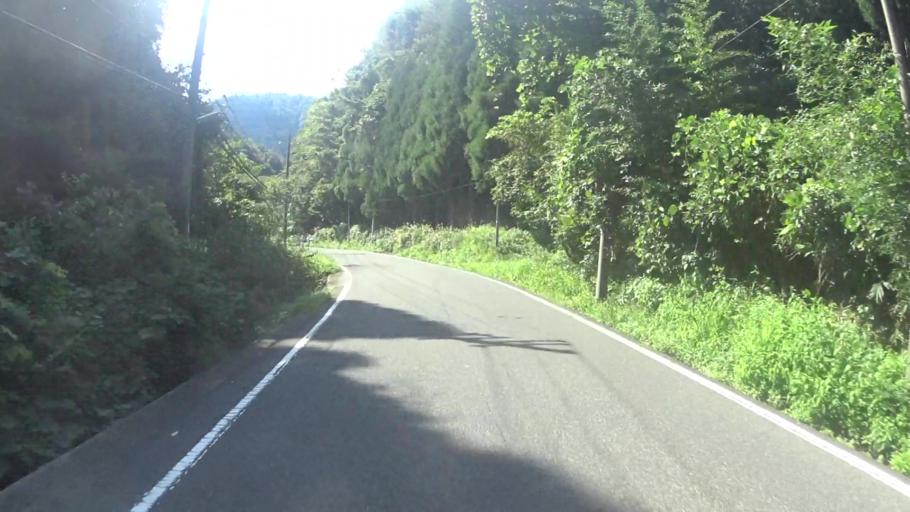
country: JP
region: Kyoto
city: Miyazu
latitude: 35.6876
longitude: 135.2869
